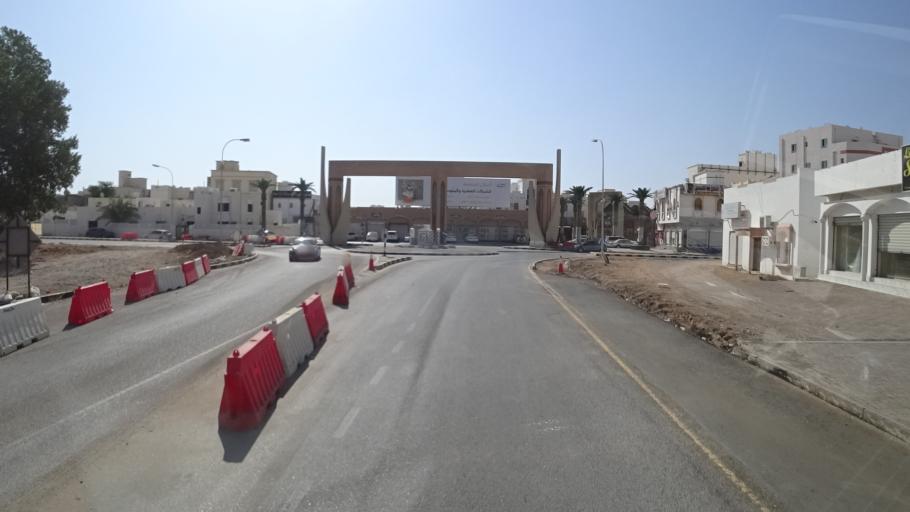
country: OM
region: Ash Sharqiyah
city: Sur
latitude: 22.5718
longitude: 59.5261
